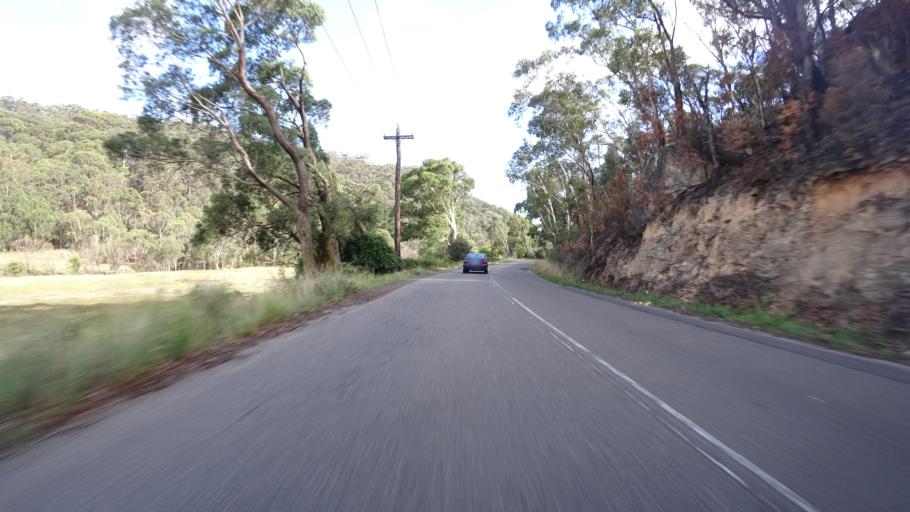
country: AU
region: New South Wales
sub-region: Lithgow
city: Lithgow
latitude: -33.4895
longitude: 150.1756
